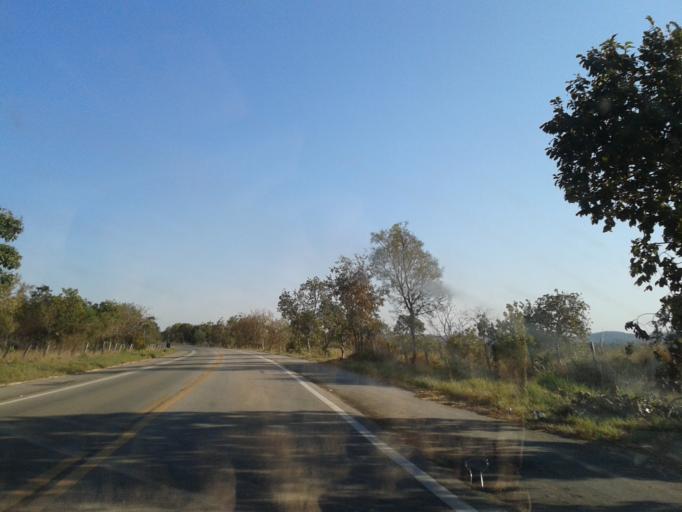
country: BR
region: Goias
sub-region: Itapuranga
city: Itapuranga
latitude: -15.3636
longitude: -50.3927
